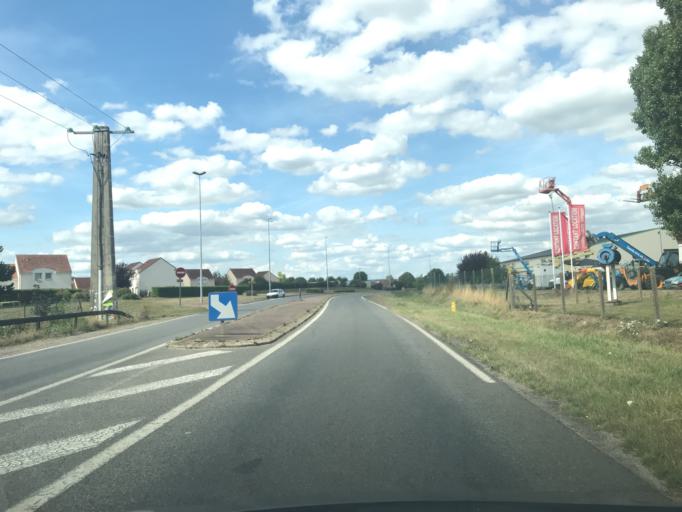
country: FR
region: Haute-Normandie
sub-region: Departement de l'Eure
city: Gaillon
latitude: 49.1666
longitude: 1.3485
